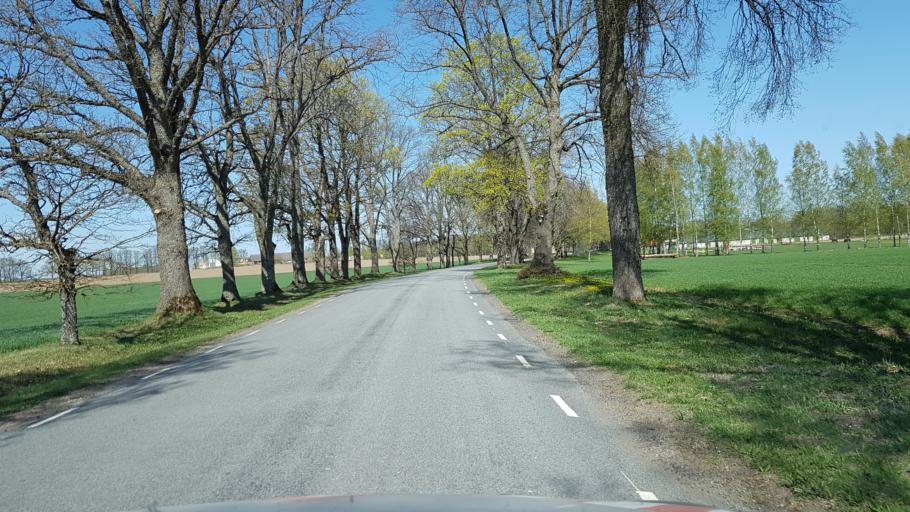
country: EE
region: Viljandimaa
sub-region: Vohma linn
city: Vohma
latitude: 58.5469
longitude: 25.5672
